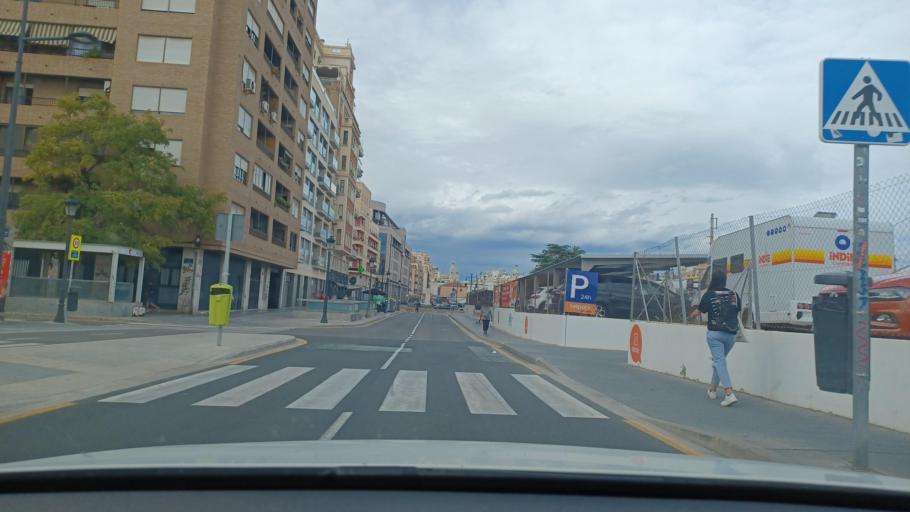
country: ES
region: Valencia
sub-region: Provincia de Valencia
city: Valencia
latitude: 39.4621
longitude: -0.3797
